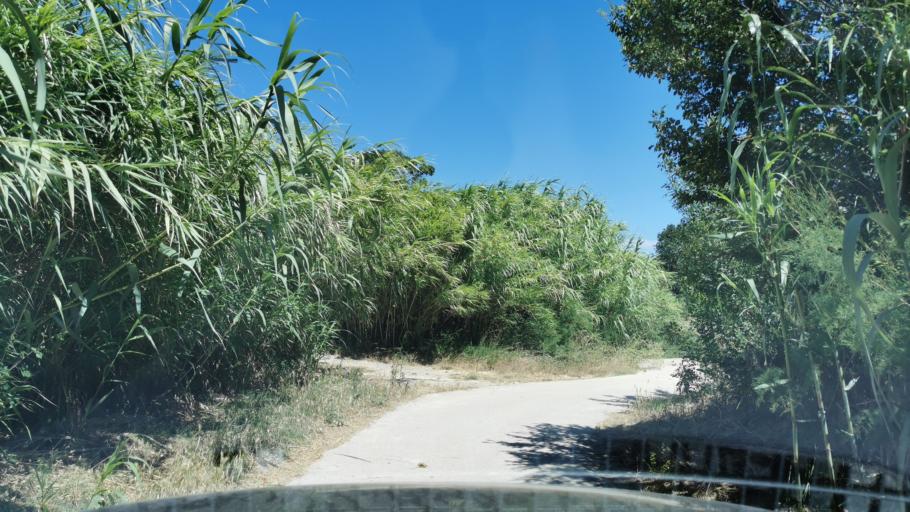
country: FR
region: Languedoc-Roussillon
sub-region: Departement de l'Aude
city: Peyriac-de-Mer
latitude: 43.1032
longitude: 2.9590
